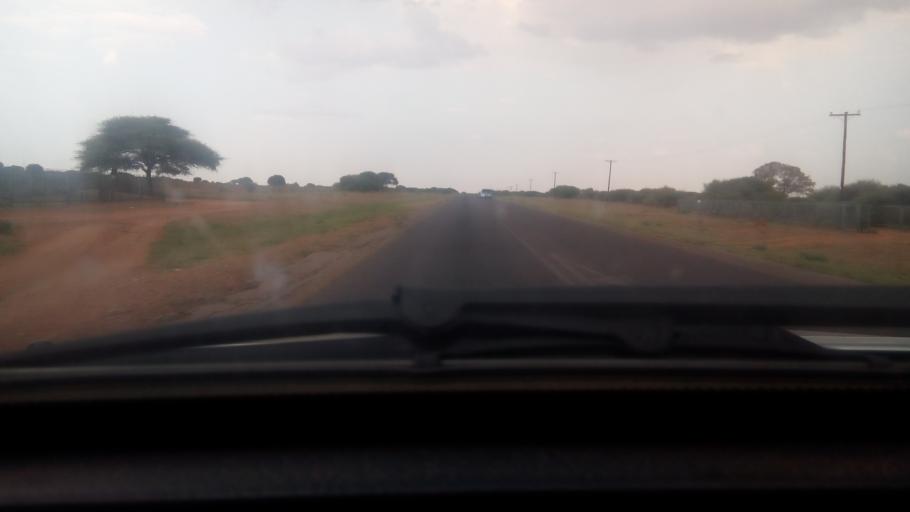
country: BW
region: Kweneng
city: Metsemotlhaba
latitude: -24.4693
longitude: 25.6852
